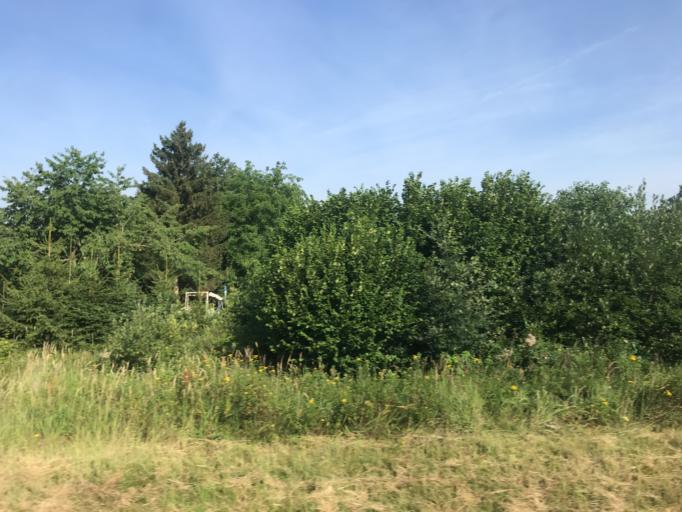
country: CZ
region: Jihocesky
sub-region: Okres Tabor
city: Tabor
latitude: 49.4343
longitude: 14.6855
